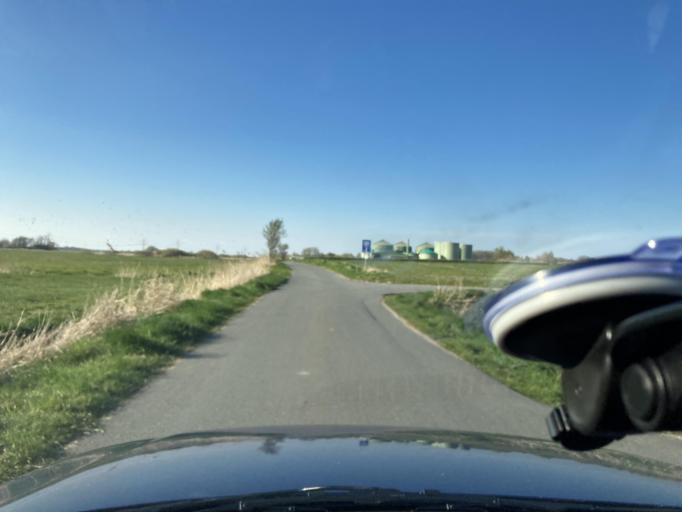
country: DE
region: Schleswig-Holstein
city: Lohe-Rickelshof
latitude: 54.1935
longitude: 9.0588
